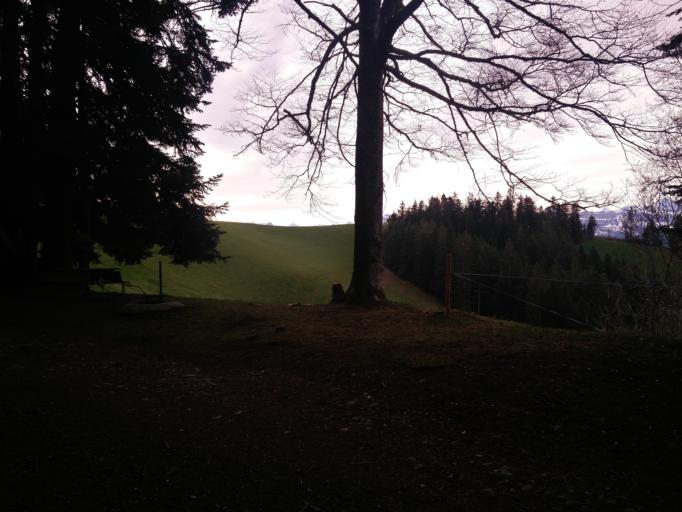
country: CH
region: Bern
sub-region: Bern-Mittelland District
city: Linden
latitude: 46.8590
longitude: 7.6673
